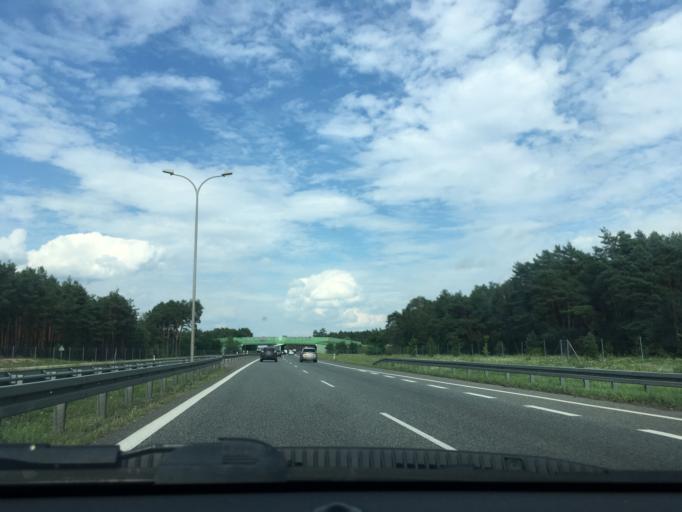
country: PL
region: Masovian Voivodeship
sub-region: Powiat wolominski
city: Tluszcz
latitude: 52.5133
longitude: 21.3977
